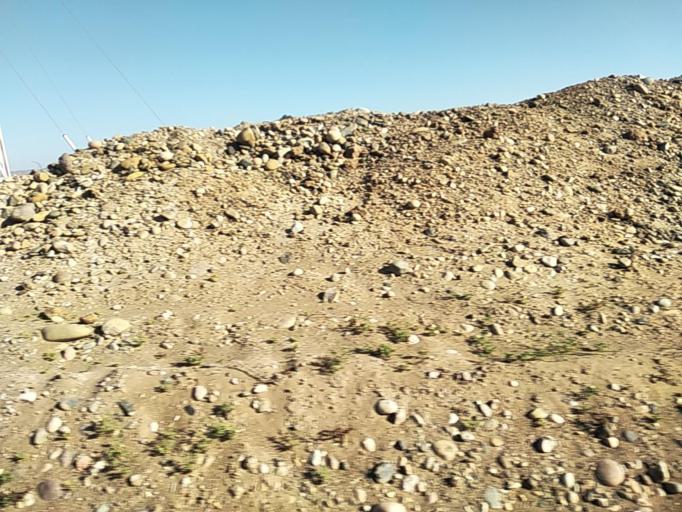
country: CL
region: Atacama
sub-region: Provincia de Copiapo
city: Copiapo
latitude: -27.3293
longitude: -70.7815
